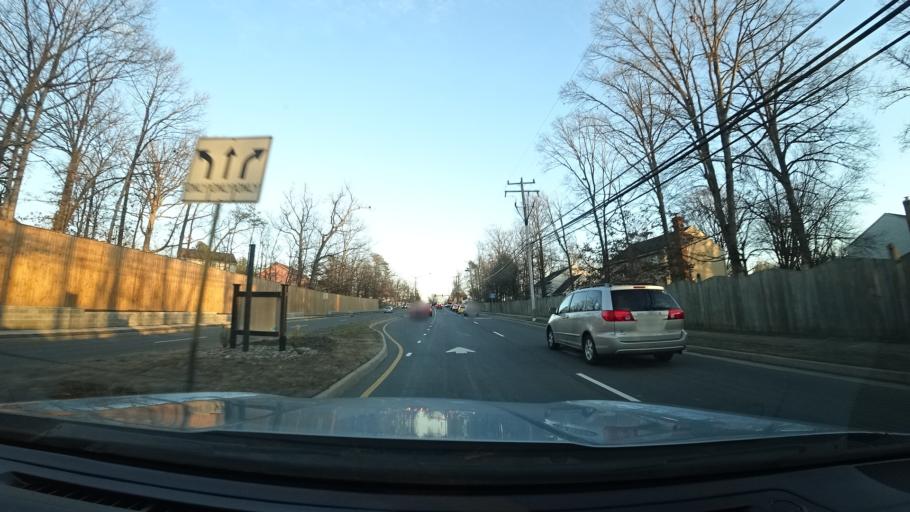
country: US
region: Virginia
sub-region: Loudoun County
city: Oak Grove
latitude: 38.9756
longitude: -77.4063
